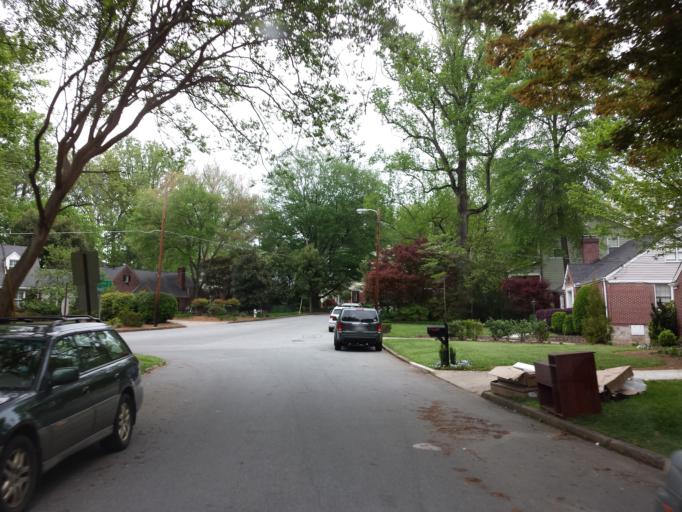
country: US
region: Georgia
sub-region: DeKalb County
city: Druid Hills
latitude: 33.7922
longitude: -84.3614
